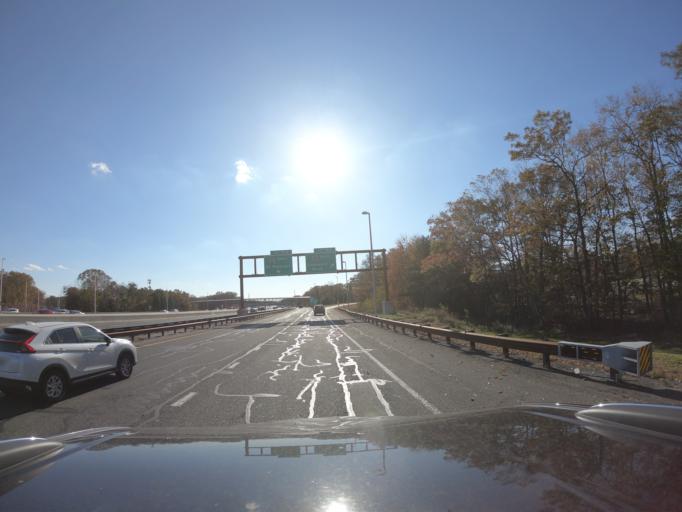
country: US
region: New Jersey
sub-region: Monmouth County
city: Ramtown
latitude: 40.1012
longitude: -74.1403
